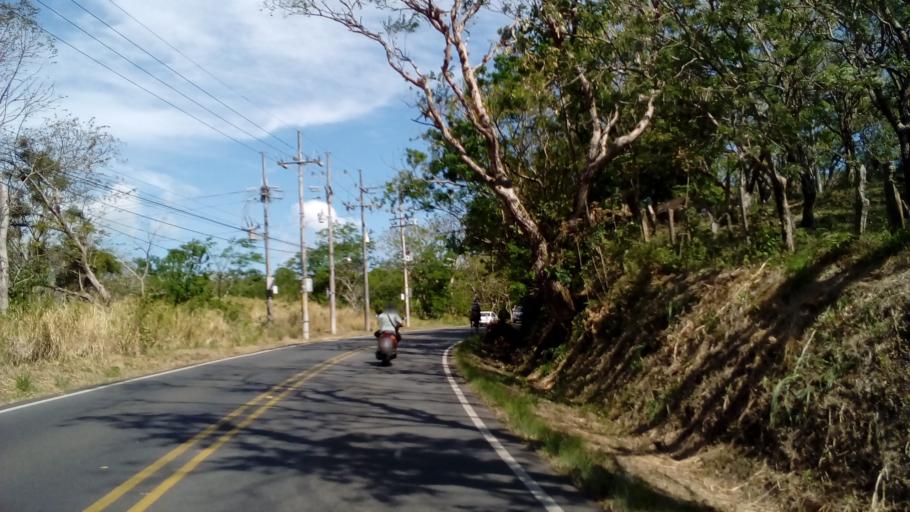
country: CR
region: Guanacaste
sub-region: Canton de Tilaran
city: Tilaran
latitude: 10.4893
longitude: -84.9839
